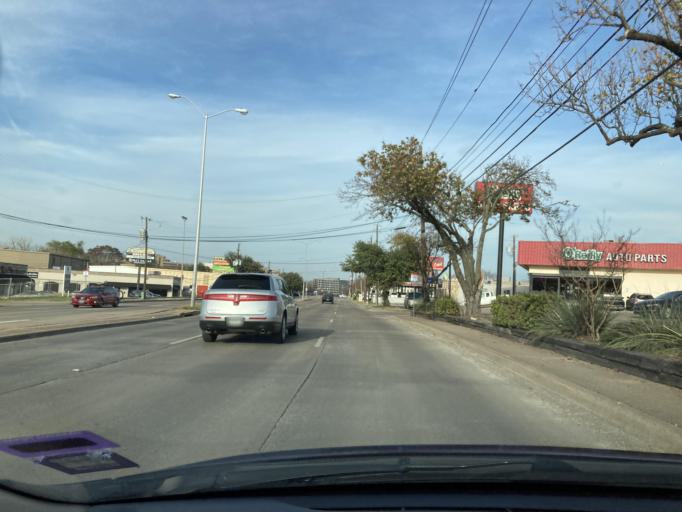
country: US
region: Texas
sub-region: Dallas County
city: University Park
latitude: 32.8735
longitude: -96.7629
